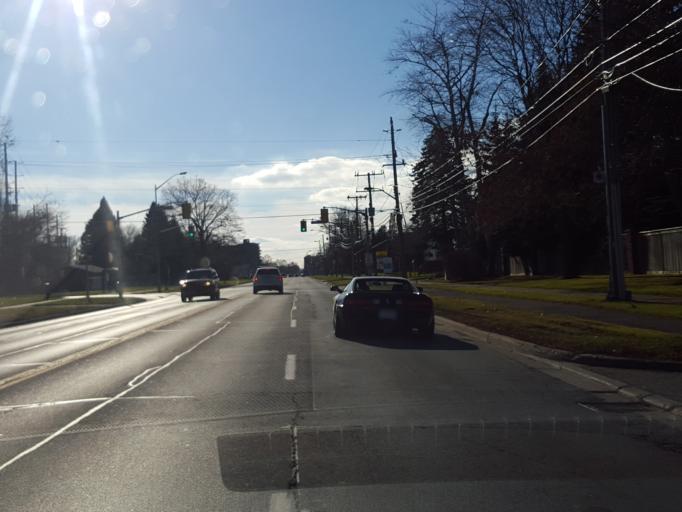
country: CA
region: Ontario
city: Burlington
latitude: 43.3419
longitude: -79.7814
